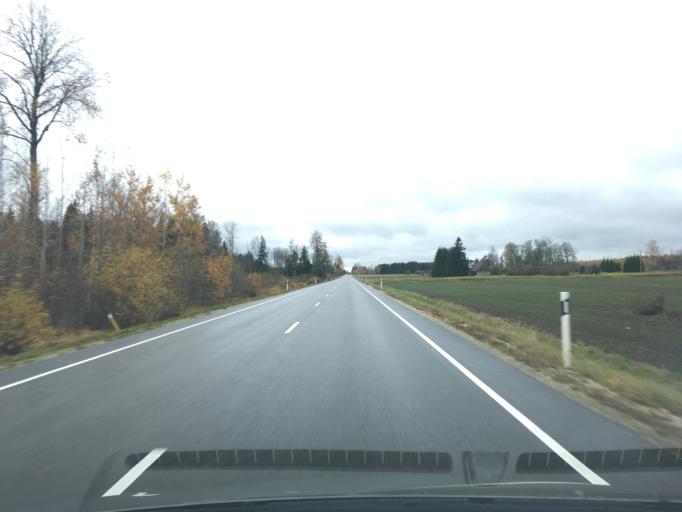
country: EE
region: Jogevamaa
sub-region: Tabivere vald
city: Tabivere
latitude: 58.4512
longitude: 26.5222
